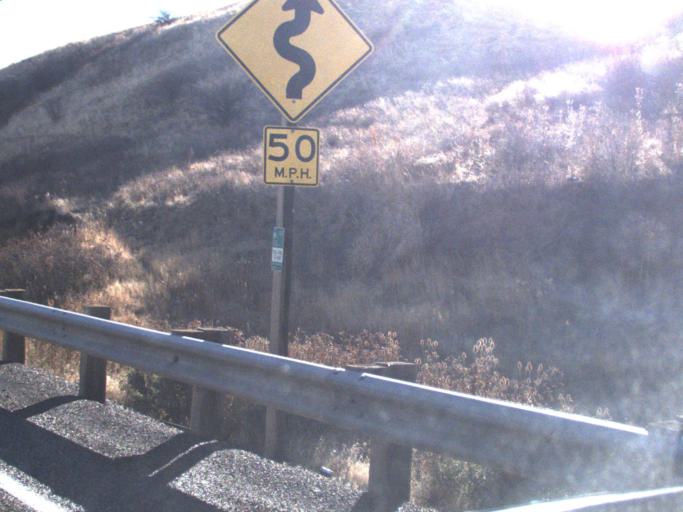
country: US
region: Washington
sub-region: Garfield County
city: Pomeroy
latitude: 46.4439
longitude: -117.3998
